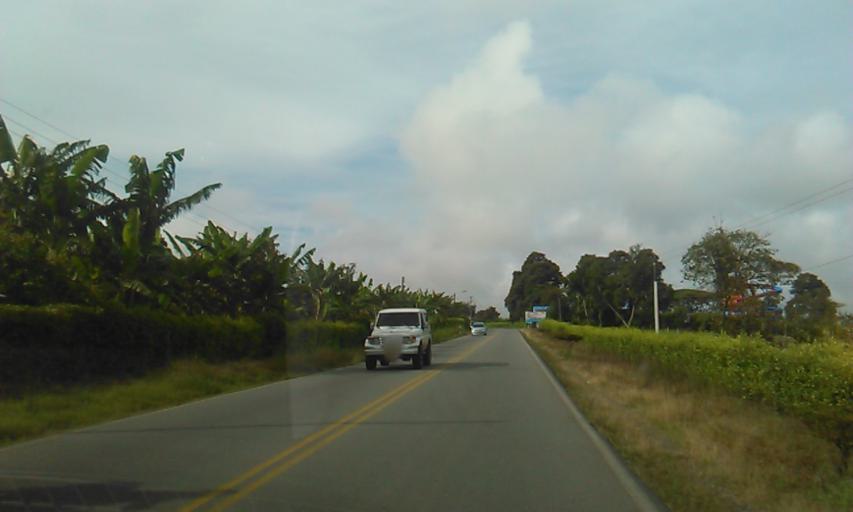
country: CO
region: Quindio
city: Armenia
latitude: 4.4651
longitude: -75.7066
